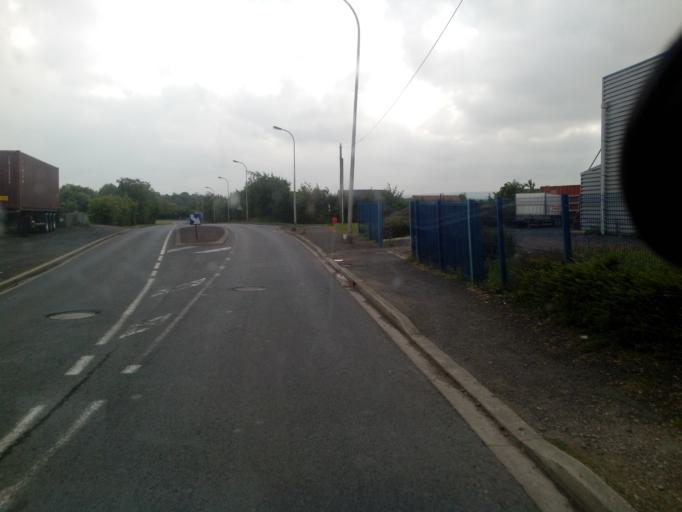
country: FR
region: Lower Normandy
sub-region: Departement du Calvados
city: Villers-Bocage
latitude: 49.0760
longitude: -0.6519
